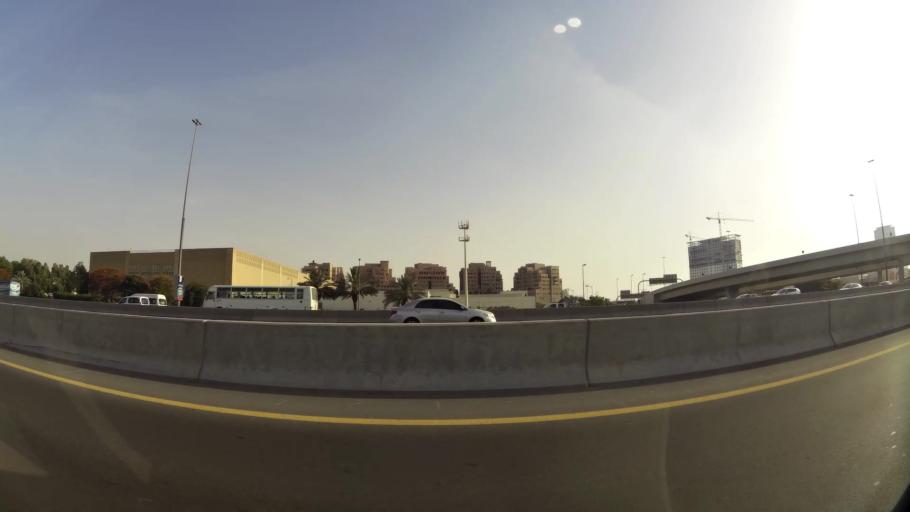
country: AE
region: Ash Shariqah
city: Sharjah
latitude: 25.2244
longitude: 55.3628
